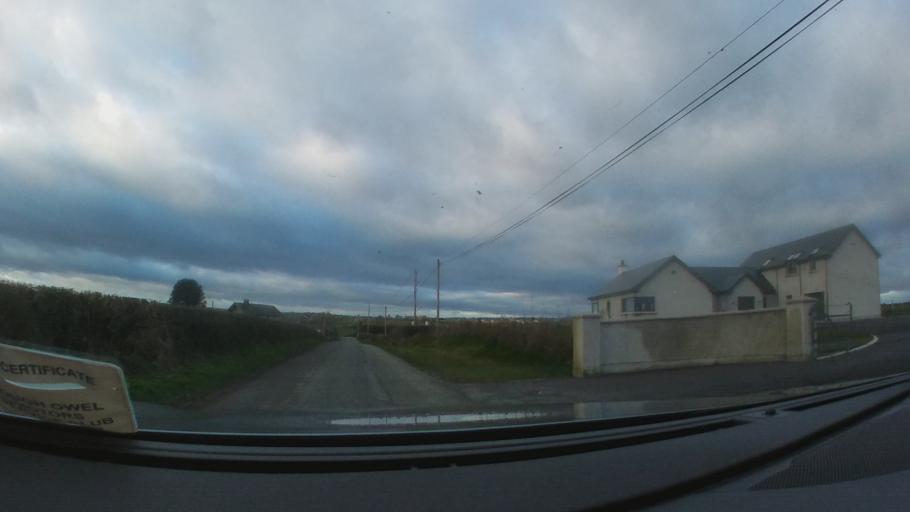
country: IE
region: Leinster
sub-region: Kilkenny
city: Thomastown
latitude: 52.5802
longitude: -7.1613
